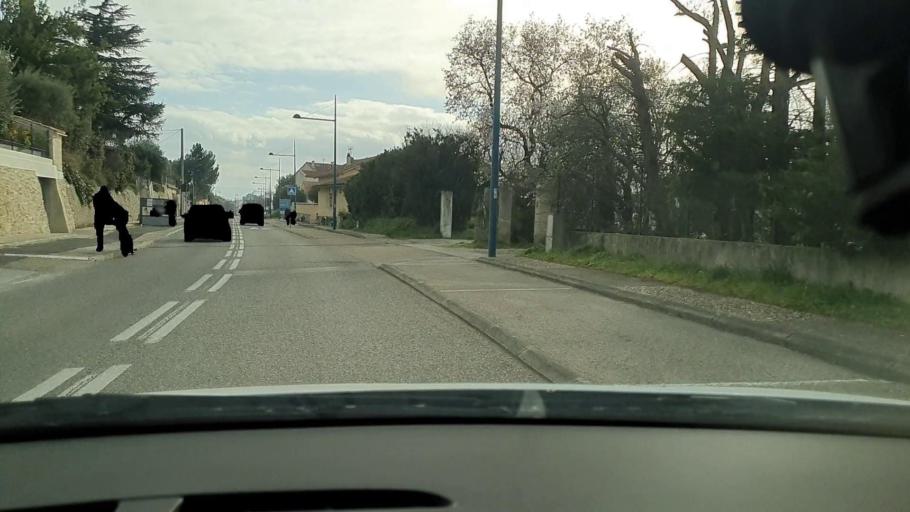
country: FR
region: Languedoc-Roussillon
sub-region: Departement du Gard
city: Beaucaire
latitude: 43.8129
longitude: 4.6328
